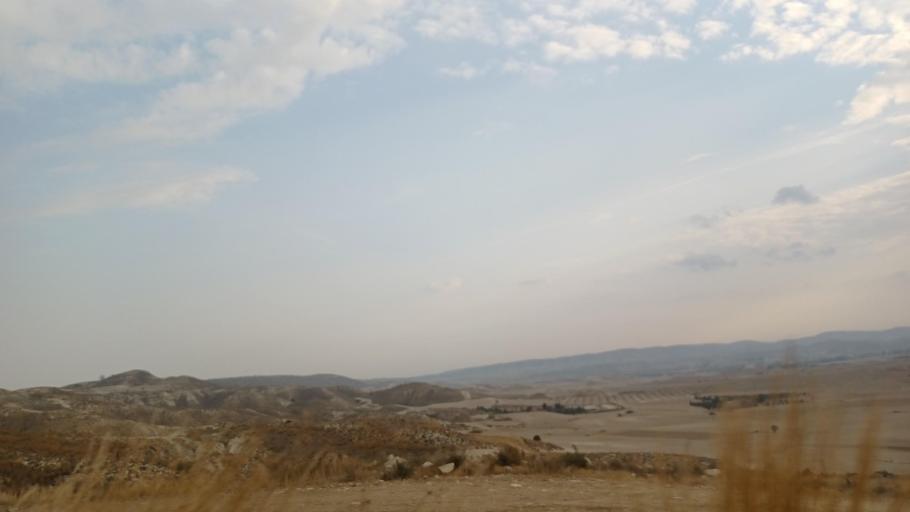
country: CY
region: Larnaka
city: Troulloi
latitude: 35.0246
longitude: 33.5741
